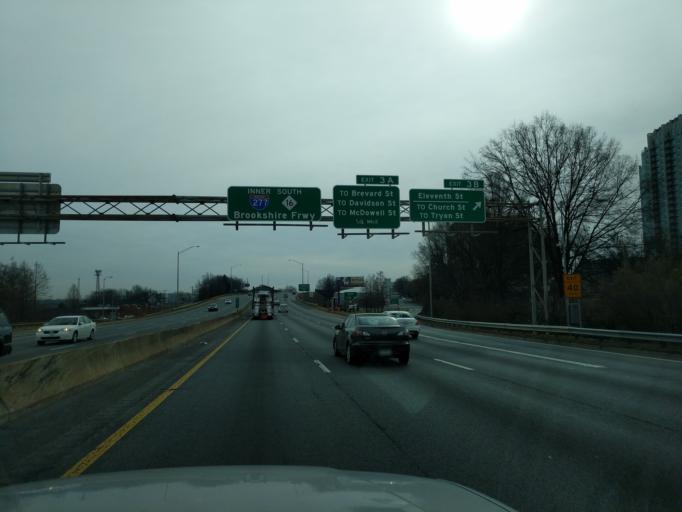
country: US
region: North Carolina
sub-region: Mecklenburg County
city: Charlotte
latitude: 35.2351
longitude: -80.8381
